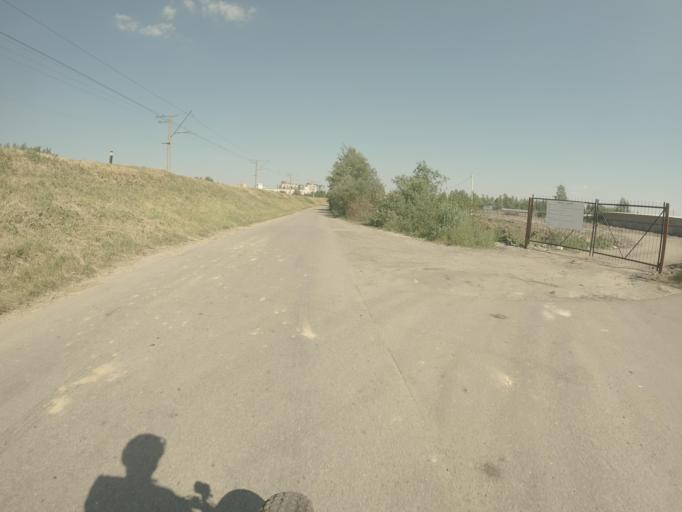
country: RU
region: Leningrad
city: Rybatskoye
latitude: 59.8366
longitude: 30.4775
